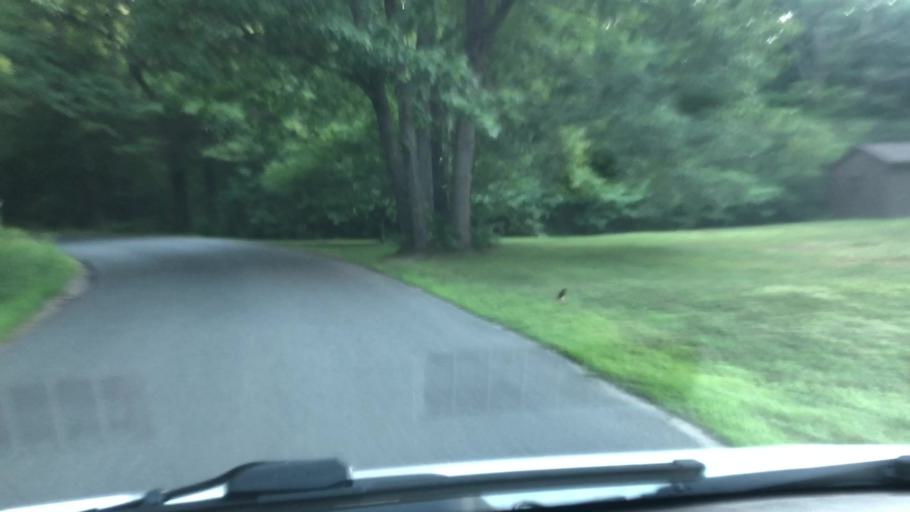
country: US
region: Massachusetts
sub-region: Hampshire County
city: Southampton
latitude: 42.2442
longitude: -72.7056
